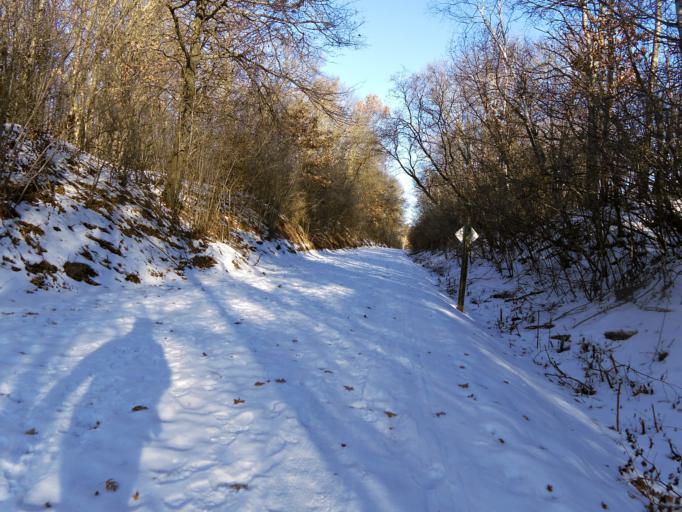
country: US
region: Minnesota
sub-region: Washington County
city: Grant
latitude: 45.0769
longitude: -92.8997
